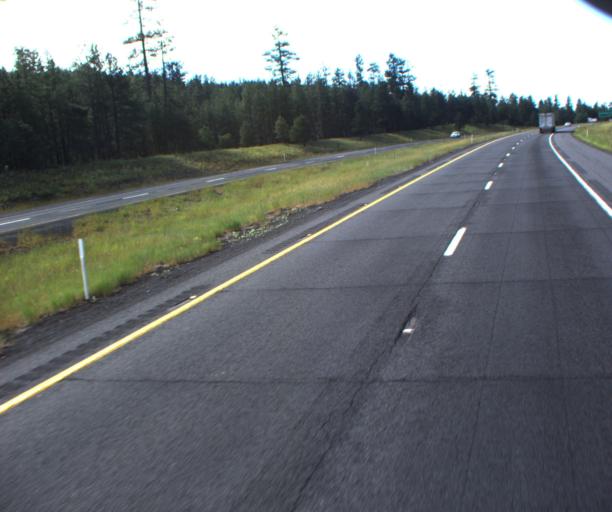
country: US
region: Arizona
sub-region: Coconino County
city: Mountainaire
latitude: 35.0366
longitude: -111.6845
